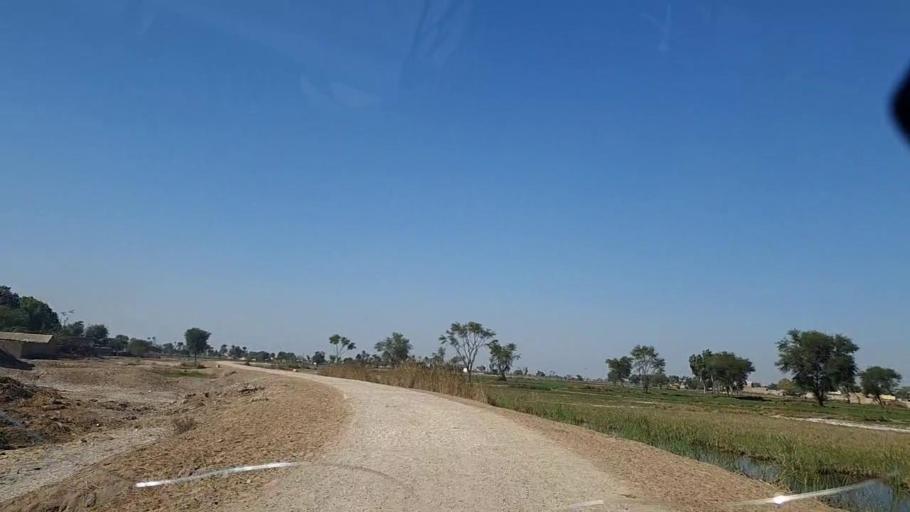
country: PK
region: Sindh
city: Khanpur
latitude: 27.8456
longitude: 69.3965
